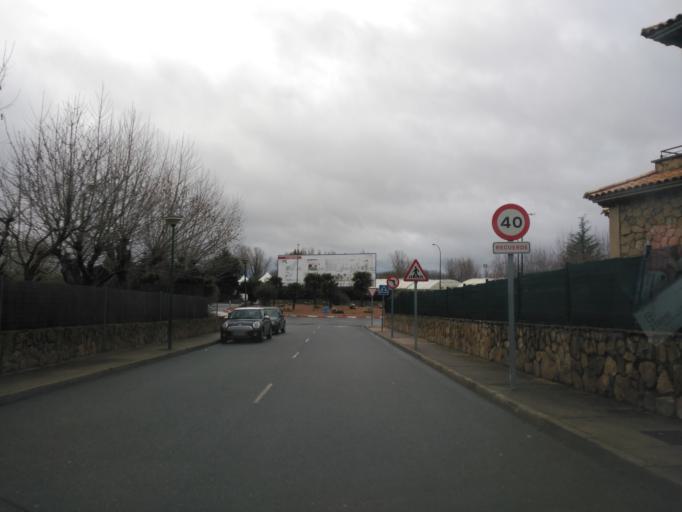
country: ES
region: Castille and Leon
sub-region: Provincia de Salamanca
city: Villamayor
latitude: 40.9840
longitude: -5.7129
